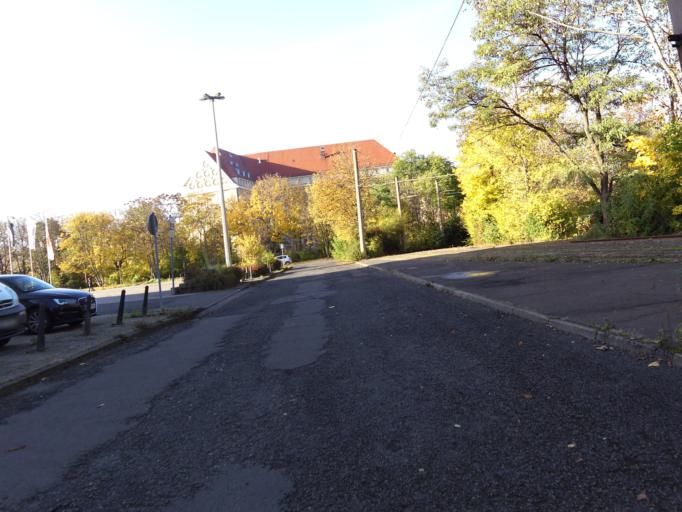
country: DE
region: Saxony
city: Leipzig
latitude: 51.3213
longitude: 12.3985
